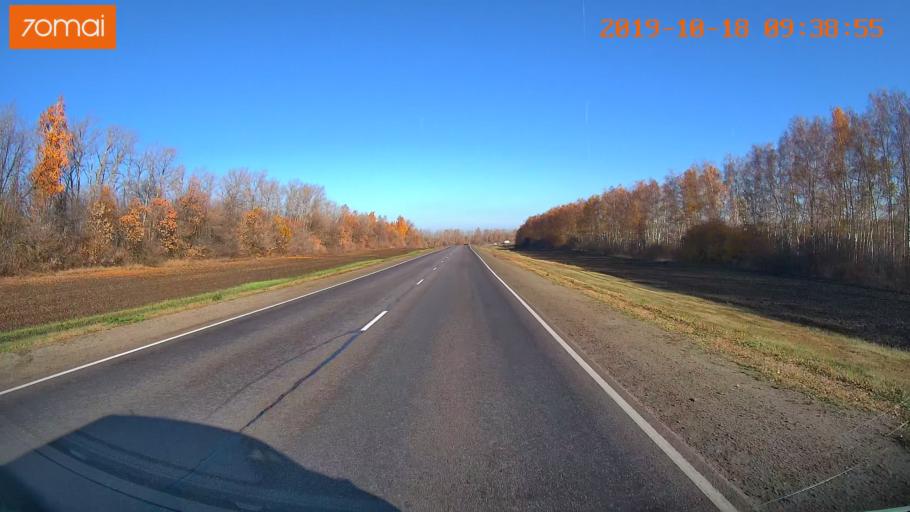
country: RU
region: Tula
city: Yefremov
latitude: 53.2454
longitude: 38.1351
